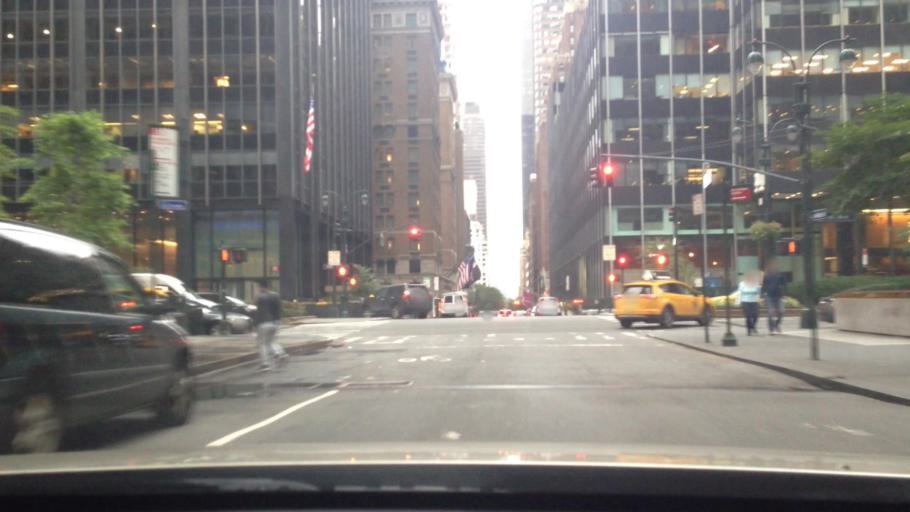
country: US
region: New York
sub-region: New York County
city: Manhattan
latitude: 40.7561
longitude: -73.9754
